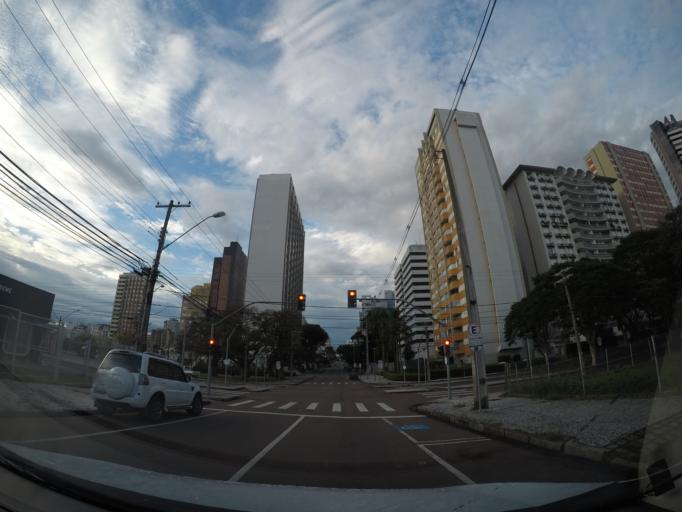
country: BR
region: Parana
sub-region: Curitiba
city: Curitiba
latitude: -25.4285
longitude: -49.2887
